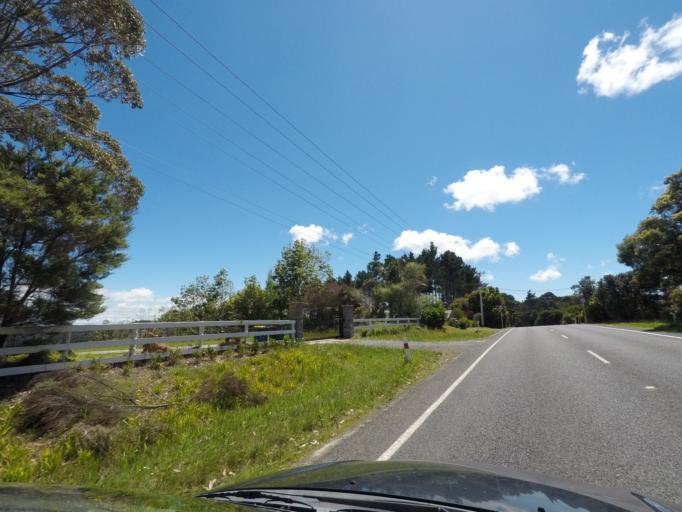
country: NZ
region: Auckland
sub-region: Auckland
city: Rothesay Bay
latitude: -36.7600
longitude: 174.6592
